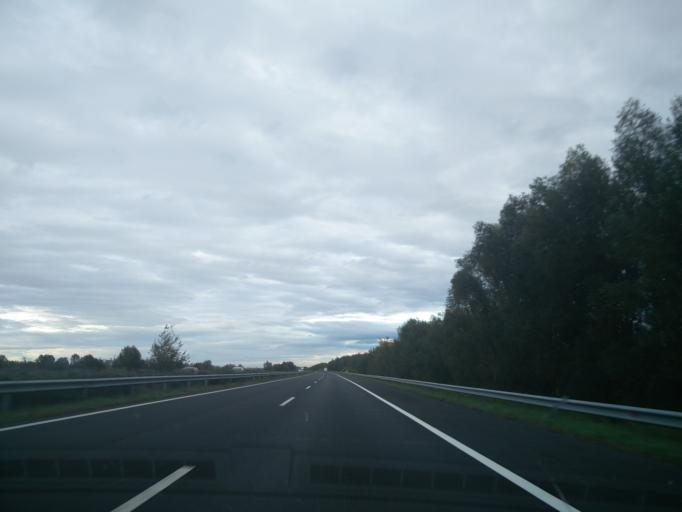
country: HU
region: Somogy
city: Kethely
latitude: 46.6901
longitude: 17.4327
